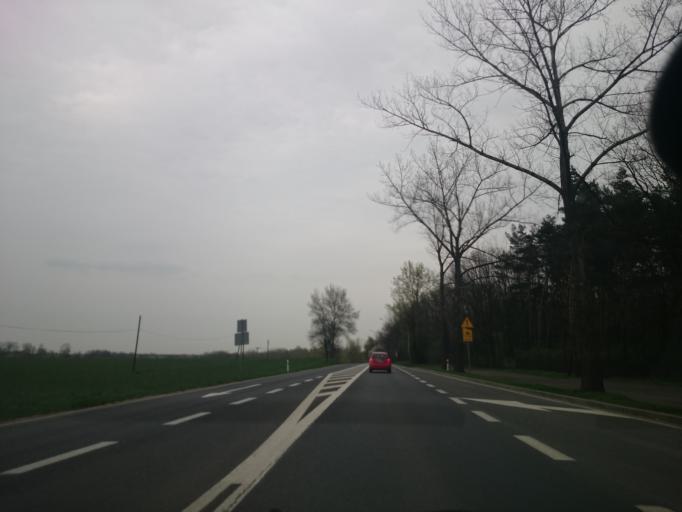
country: PL
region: Opole Voivodeship
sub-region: Powiat nyski
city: Nysa
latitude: 50.4781
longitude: 17.2801
